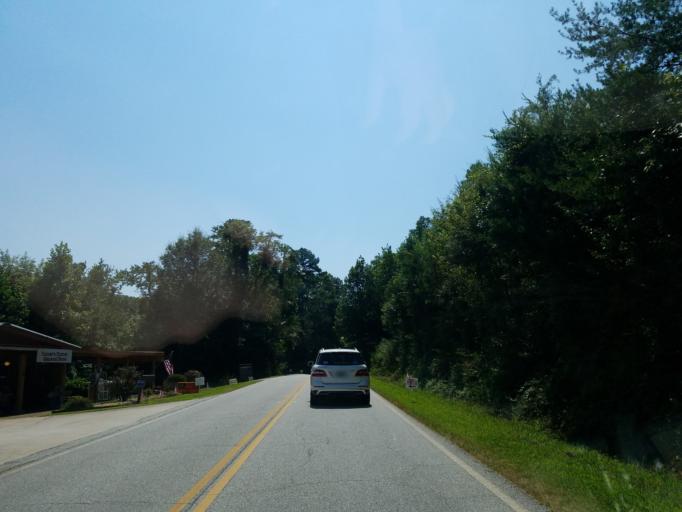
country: US
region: Georgia
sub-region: Lumpkin County
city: Dahlonega
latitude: 34.6603
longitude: -83.9047
